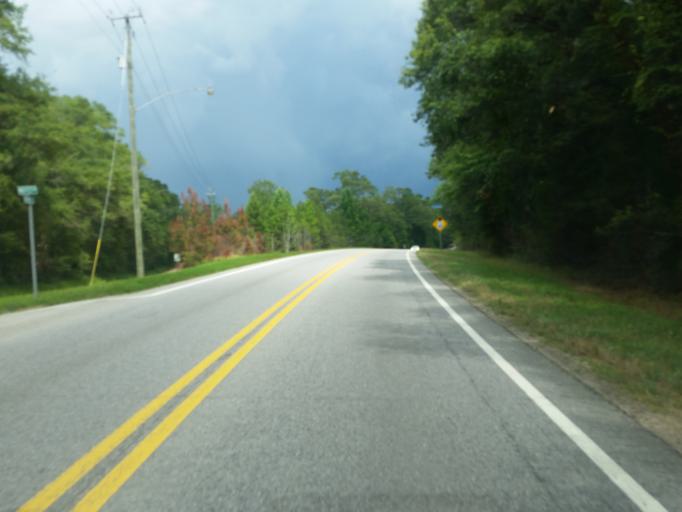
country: US
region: Mississippi
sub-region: Jackson County
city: Hurley
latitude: 30.8257
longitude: -88.3687
